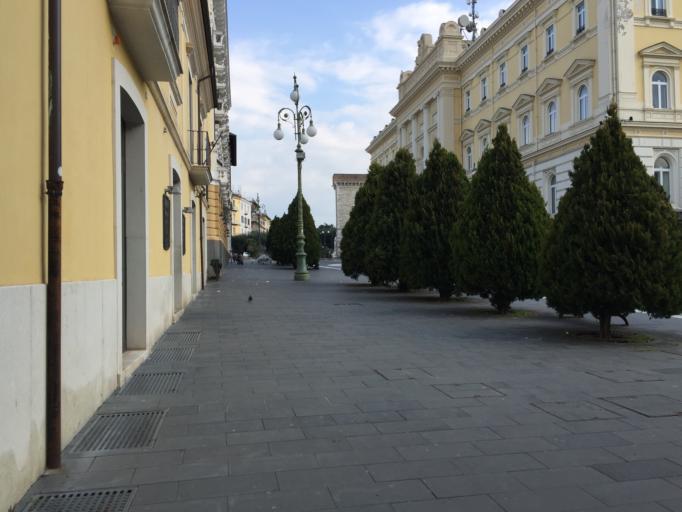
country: IT
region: Campania
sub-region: Provincia di Benevento
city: Benevento
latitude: 41.1303
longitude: 14.7811
